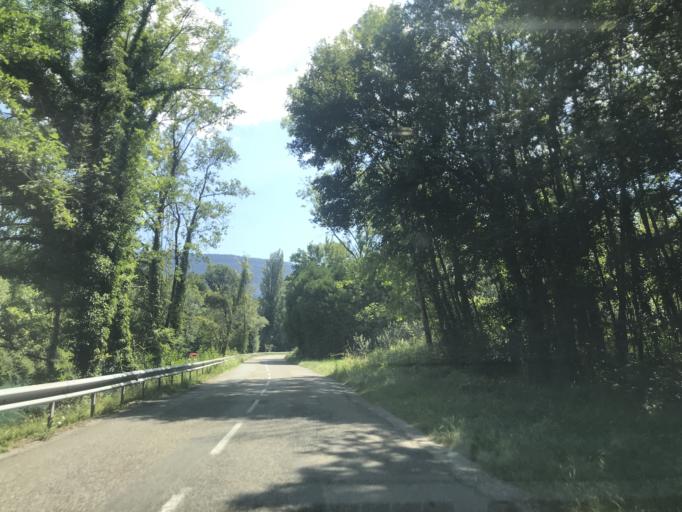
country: FR
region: Rhone-Alpes
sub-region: Departement de la Savoie
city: Chatillon
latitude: 45.8164
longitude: 5.8108
